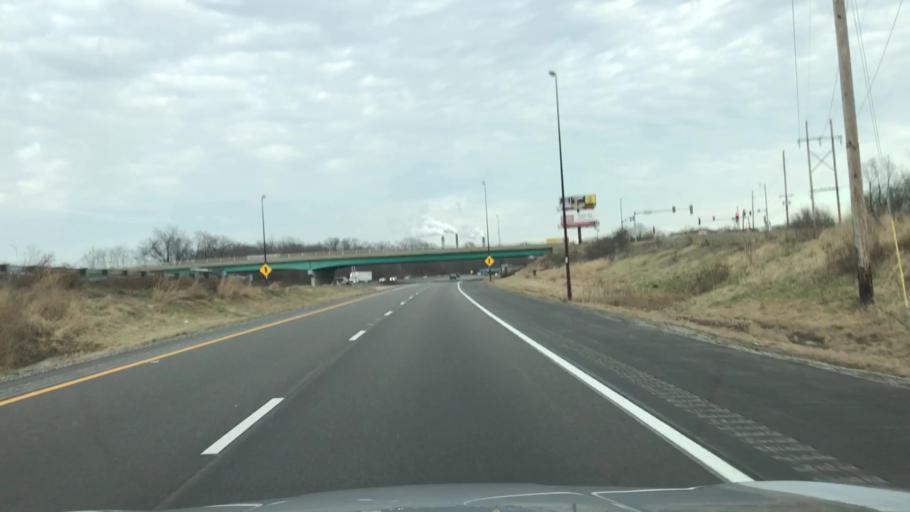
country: US
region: Illinois
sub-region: Sangamon County
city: Southern View
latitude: 39.7426
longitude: -89.6378
